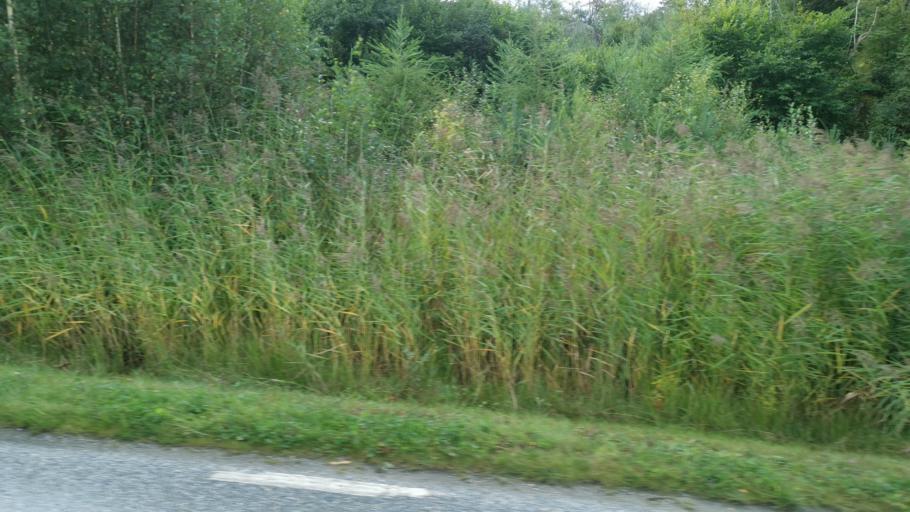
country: SE
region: Vaestra Goetaland
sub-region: Tjorns Kommun
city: Skaerhamn
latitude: 58.0406
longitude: 11.6116
